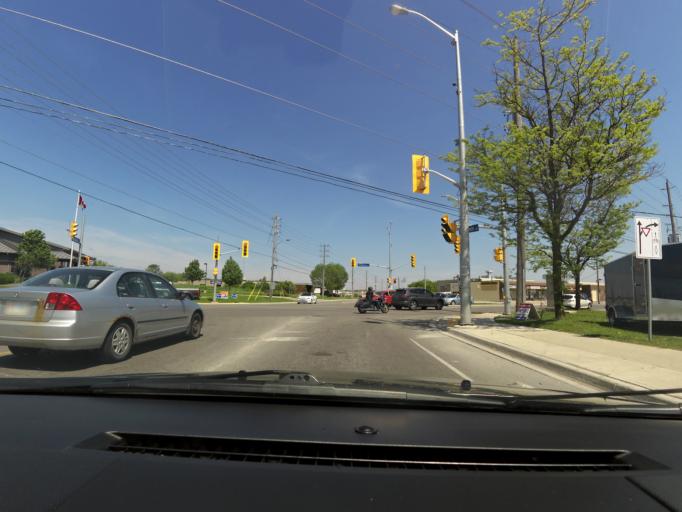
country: CA
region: Ontario
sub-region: Wellington County
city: Guelph
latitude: 43.5554
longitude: -80.2291
